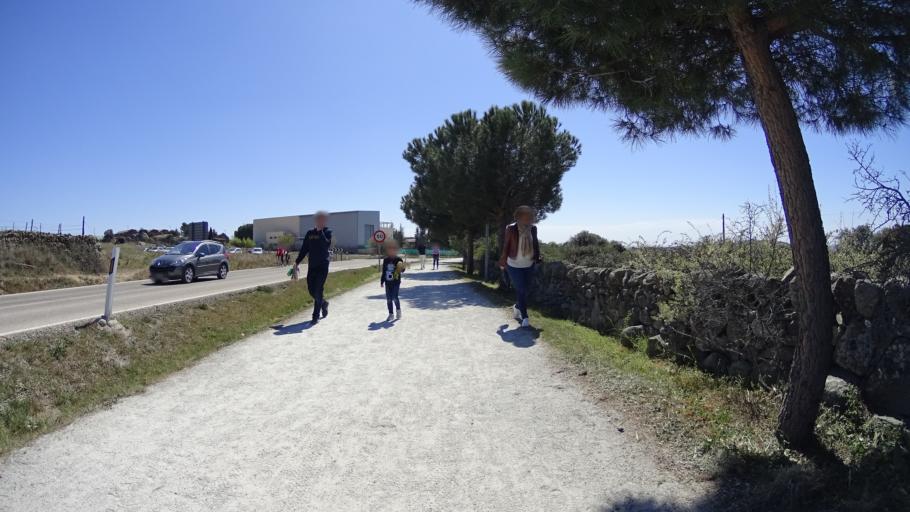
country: ES
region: Madrid
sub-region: Provincia de Madrid
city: Colmenar Viejo
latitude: 40.7010
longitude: -3.7681
